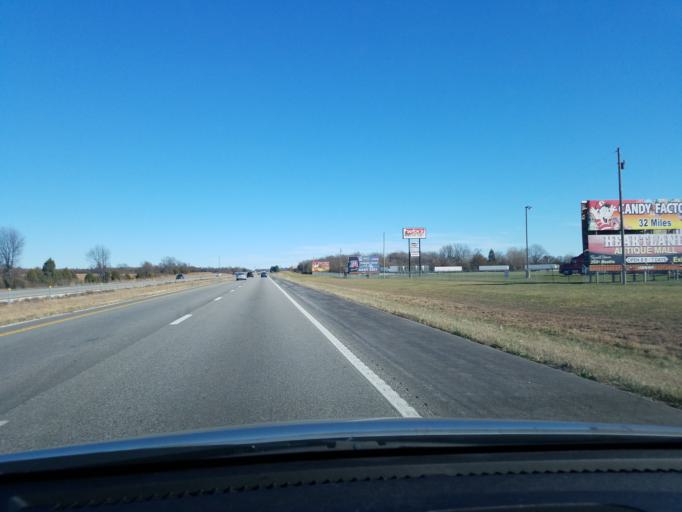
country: US
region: Missouri
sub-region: Greene County
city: Strafford
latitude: 37.2571
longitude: -93.1628
